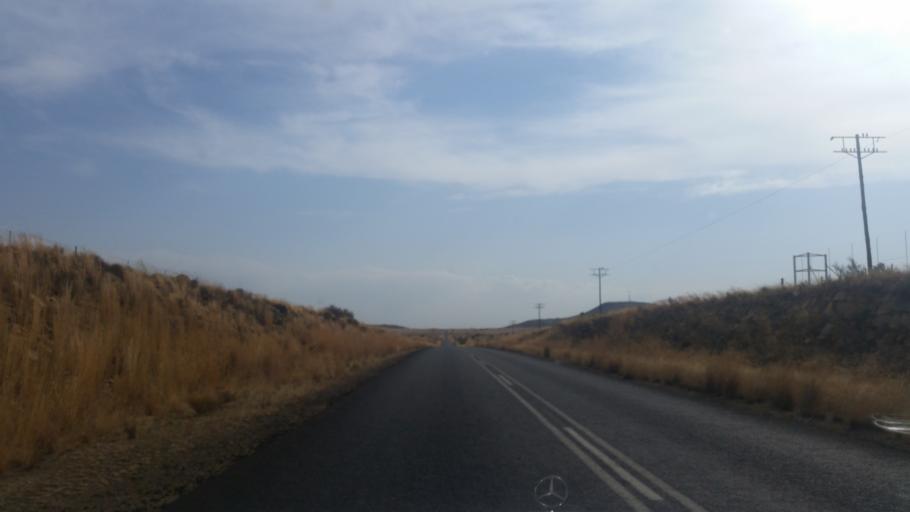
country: ZA
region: Orange Free State
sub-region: Xhariep District Municipality
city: Trompsburg
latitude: -30.4665
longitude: 26.0475
